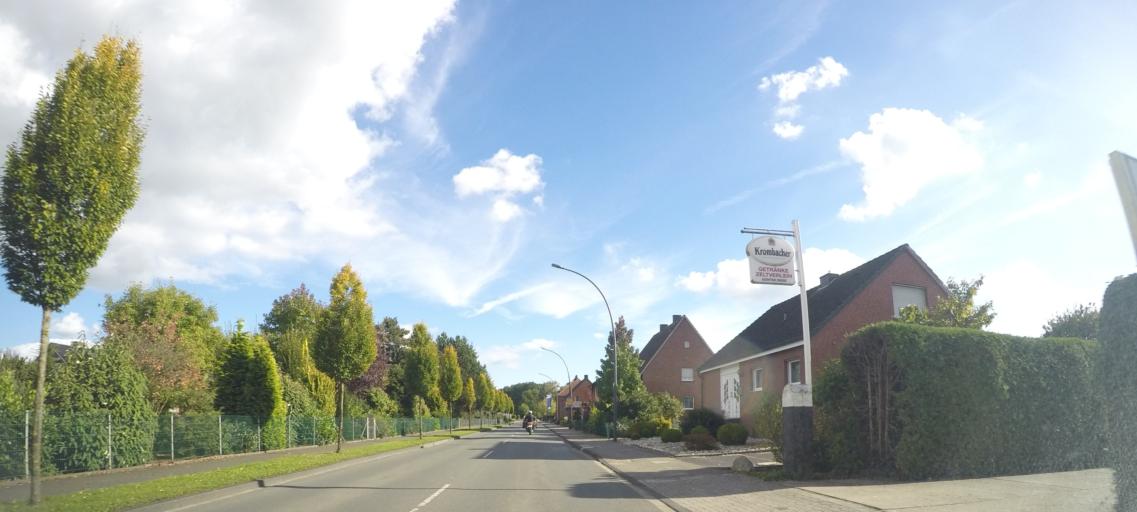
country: DE
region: North Rhine-Westphalia
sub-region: Regierungsbezirk Arnsberg
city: Welver
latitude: 51.6628
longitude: 8.0448
